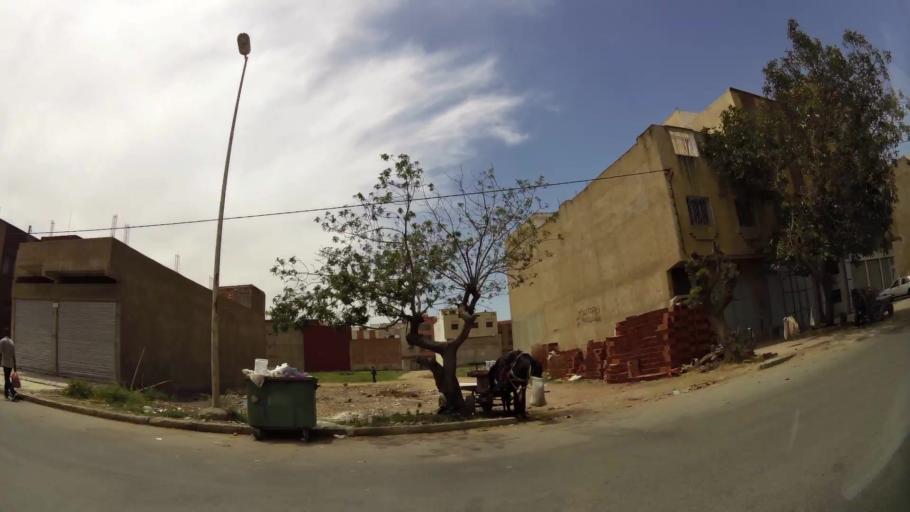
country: MA
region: Rabat-Sale-Zemmour-Zaer
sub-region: Khemisset
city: Khemisset
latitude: 33.8252
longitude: -6.0773
